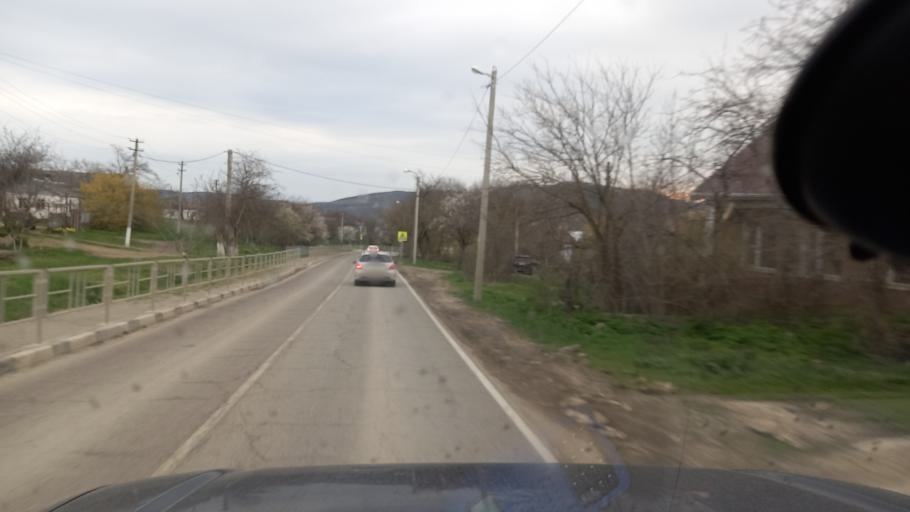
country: RU
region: Krasnodarskiy
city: Anapskaya
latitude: 44.8429
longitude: 37.3886
